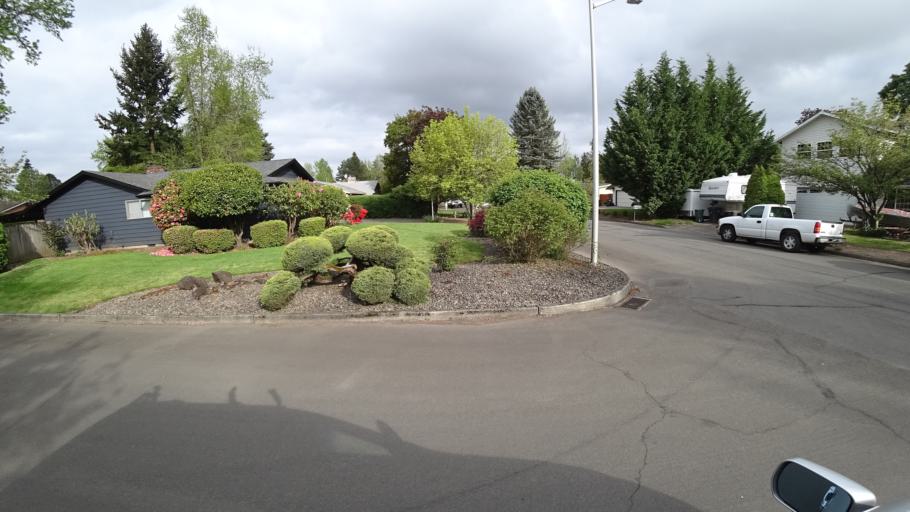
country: US
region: Oregon
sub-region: Washington County
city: Hillsboro
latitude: 45.5309
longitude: -122.9687
